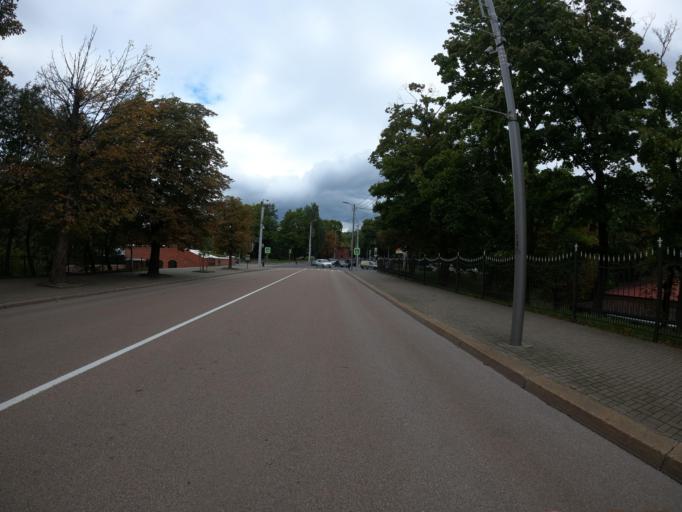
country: RU
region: Kaliningrad
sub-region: Gorod Kaliningrad
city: Kaliningrad
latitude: 54.7118
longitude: 20.4909
